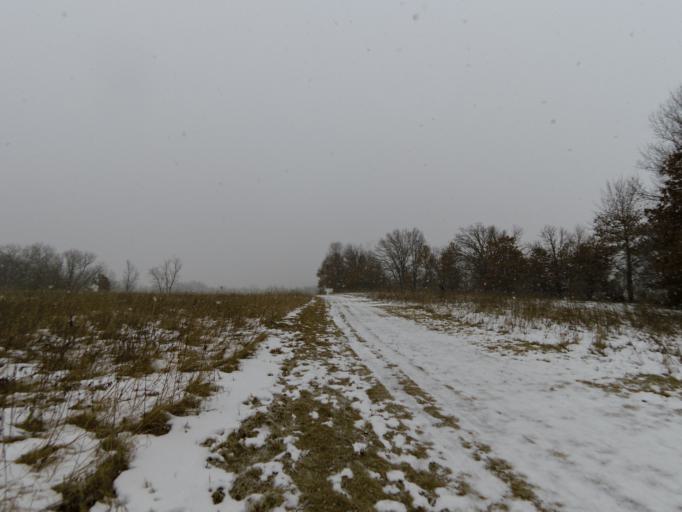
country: US
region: Minnesota
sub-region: Washington County
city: Lake Elmo
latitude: 44.9808
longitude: -92.9110
